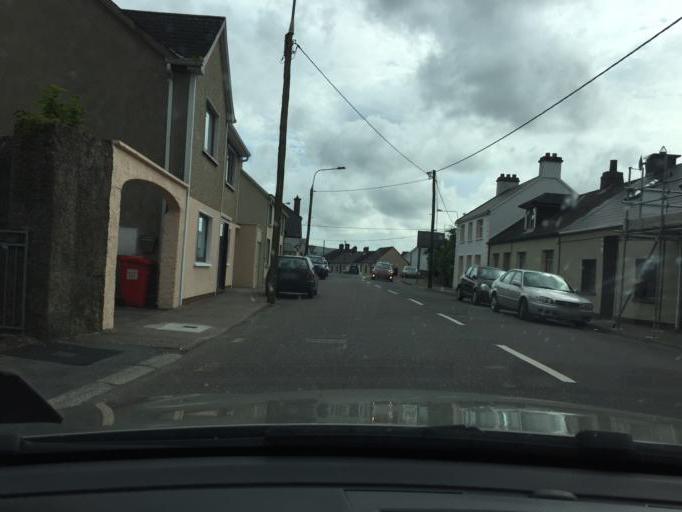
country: IE
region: Munster
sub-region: Waterford
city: Dungarvan
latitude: 52.0939
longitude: -7.6128
